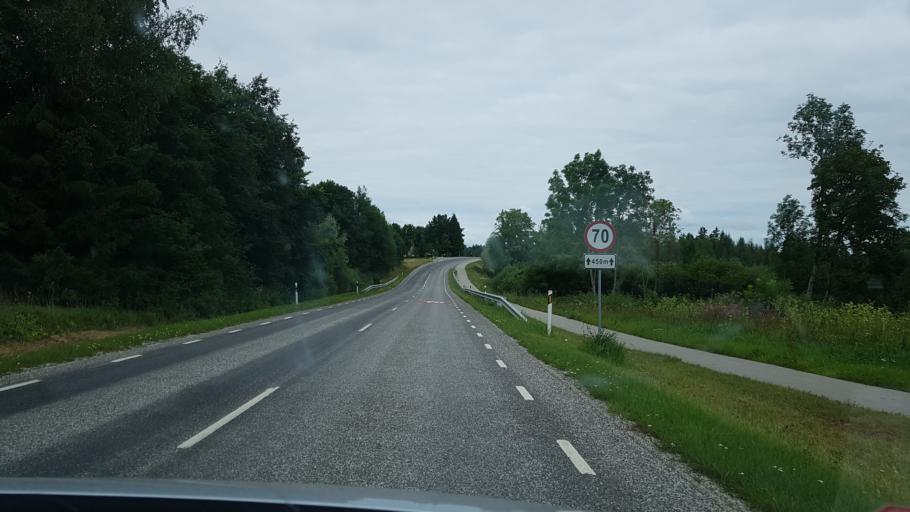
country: EE
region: Vorumaa
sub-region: Antsla vald
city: Vana-Antsla
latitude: 58.0510
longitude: 26.5382
